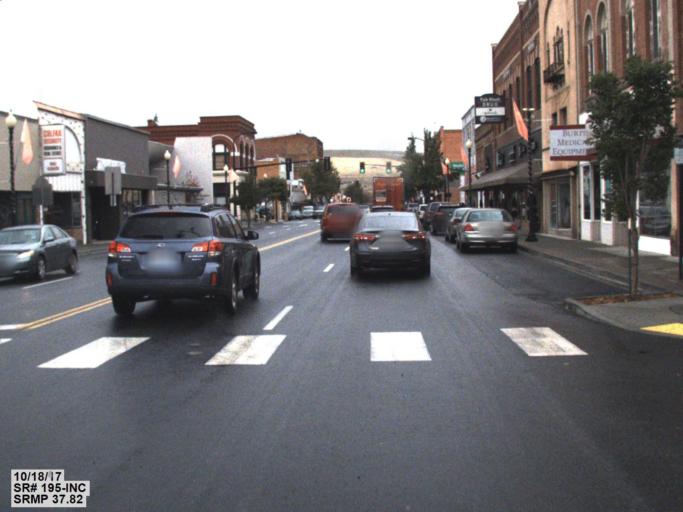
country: US
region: Washington
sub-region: Whitman County
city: Colfax
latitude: 46.8800
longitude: -117.3647
